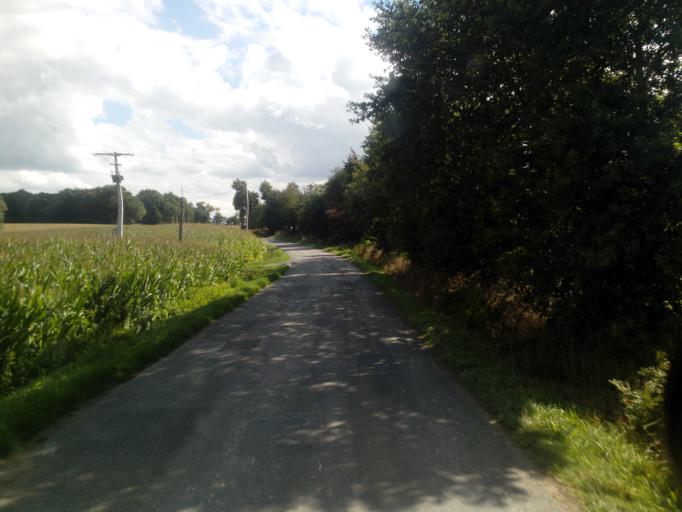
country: FR
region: Brittany
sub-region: Departement d'Ille-et-Vilaine
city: Gael
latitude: 48.1146
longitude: -2.1393
